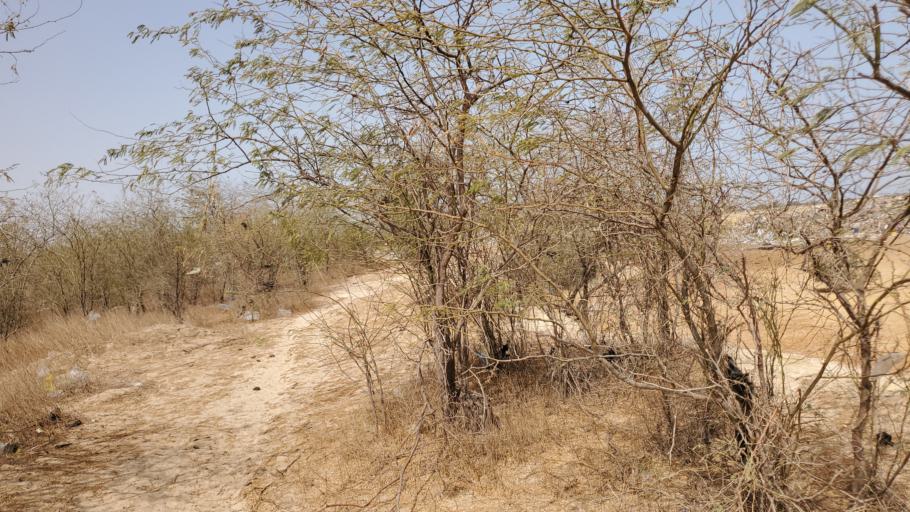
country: SN
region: Saint-Louis
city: Saint-Louis
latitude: 15.9490
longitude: -16.4294
